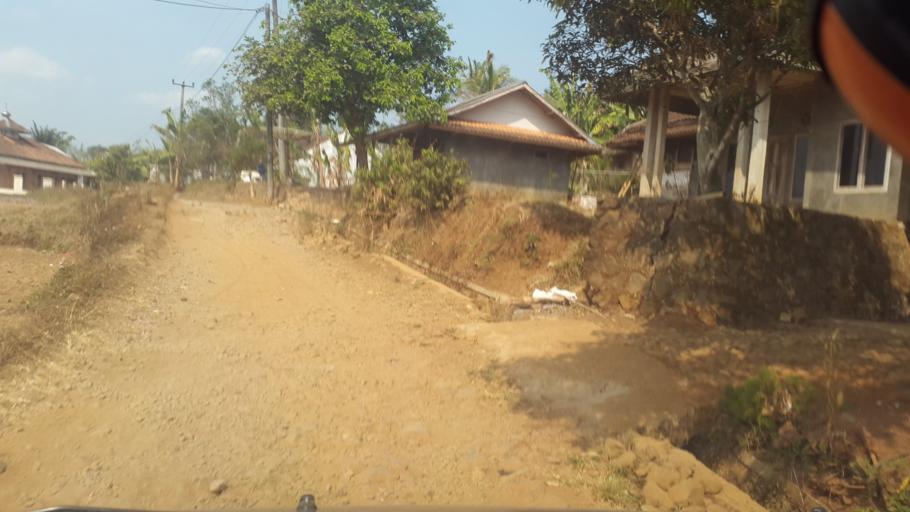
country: ID
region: West Java
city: Nangerang
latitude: -7.1122
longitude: 106.8019
